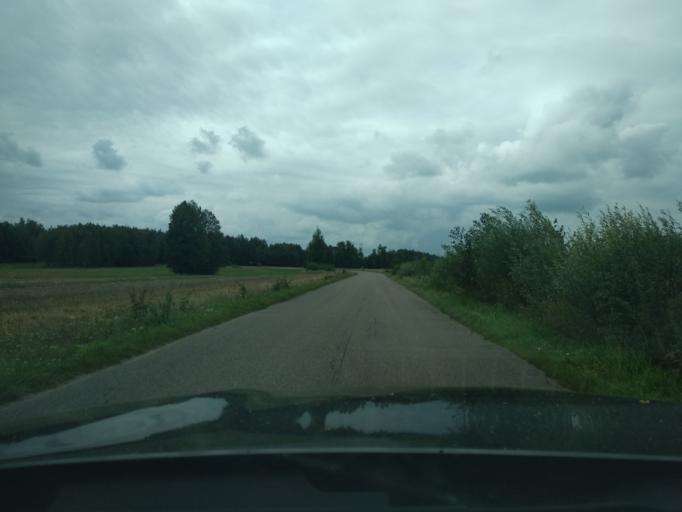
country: PL
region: Masovian Voivodeship
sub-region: Powiat pultuski
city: Obryte
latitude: 52.7462
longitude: 21.2151
